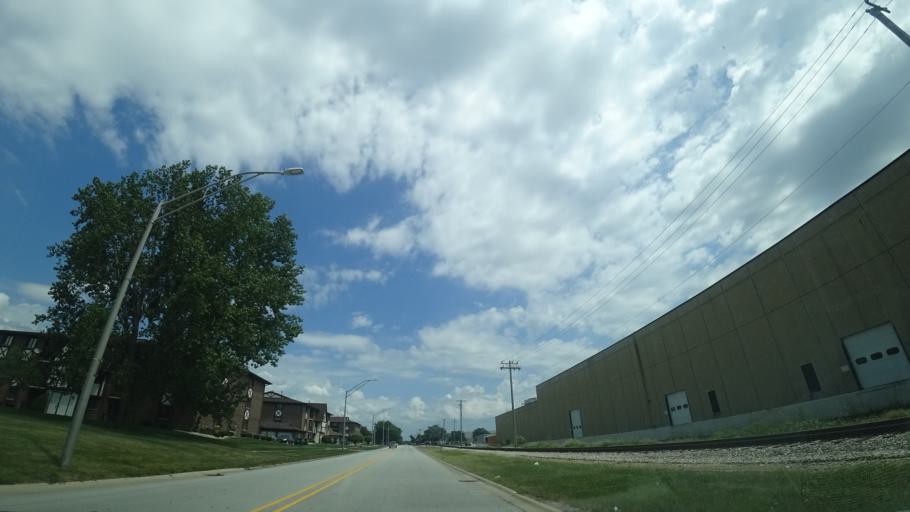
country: US
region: Illinois
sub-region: Cook County
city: Crestwood
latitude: 41.6706
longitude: -87.7512
